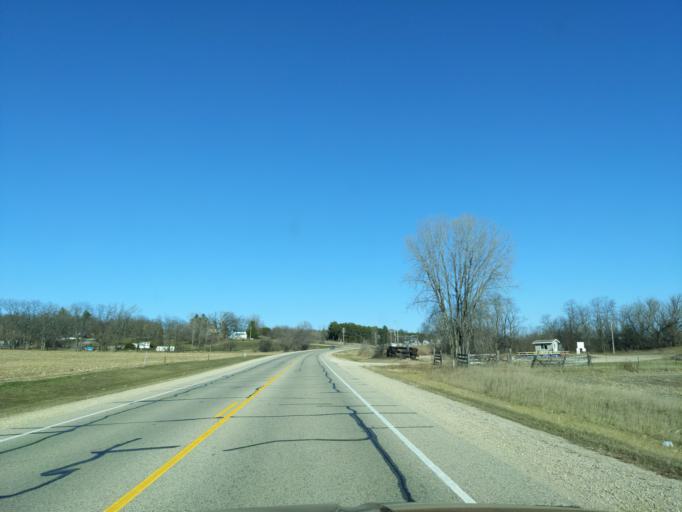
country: US
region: Wisconsin
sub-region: Waushara County
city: Wautoma
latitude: 44.1023
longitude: -89.2888
